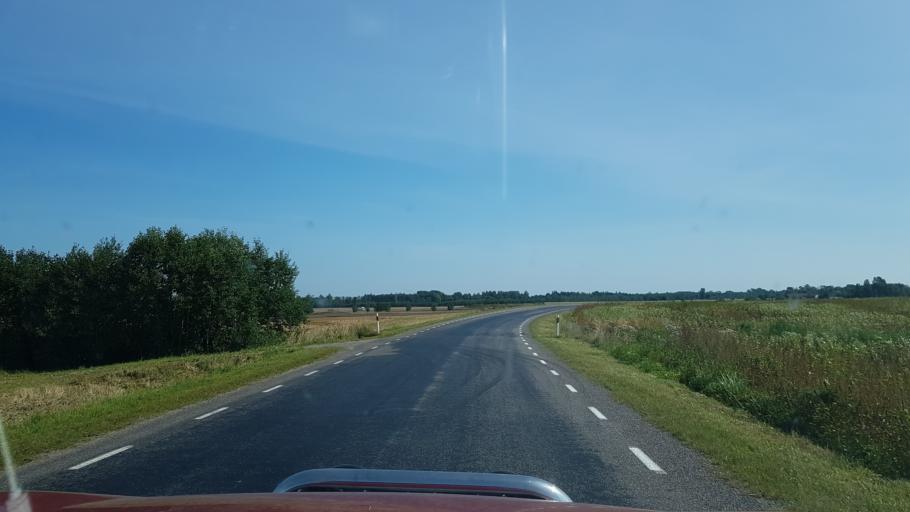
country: EE
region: Viljandimaa
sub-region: Viiratsi vald
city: Viiratsi
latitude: 58.5082
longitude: 25.6790
